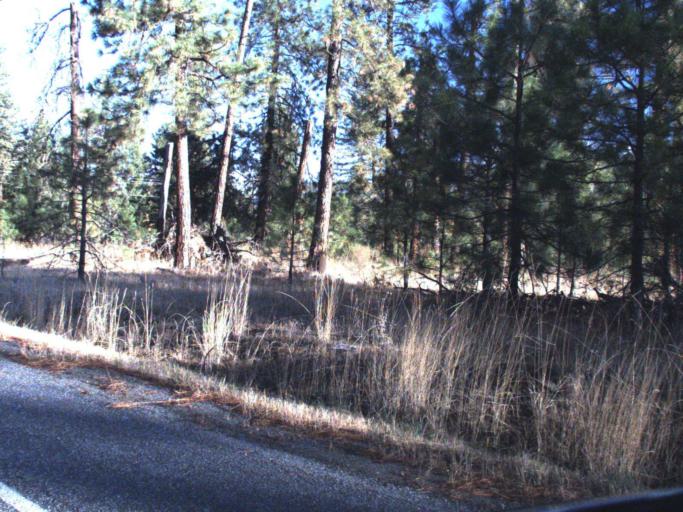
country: US
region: Washington
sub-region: Okanogan County
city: Coulee Dam
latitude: 48.0995
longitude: -118.6955
